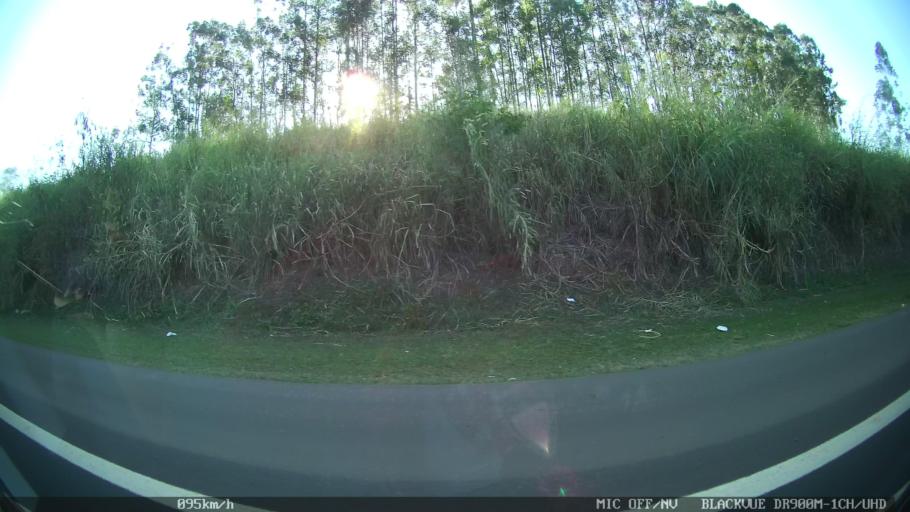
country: BR
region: Sao Paulo
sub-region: Piracicaba
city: Piracicaba
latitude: -22.6998
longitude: -47.6410
